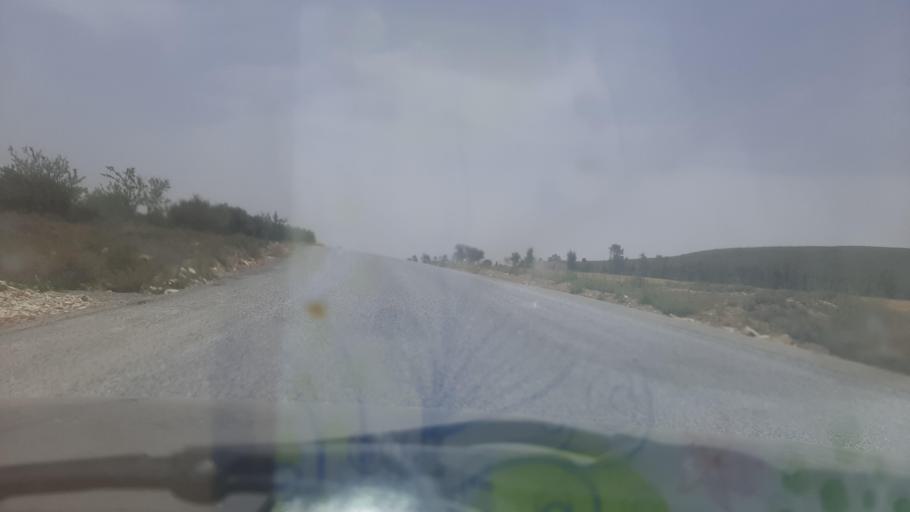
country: TN
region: Tunis
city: La Mohammedia
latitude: 36.5460
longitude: 10.1515
